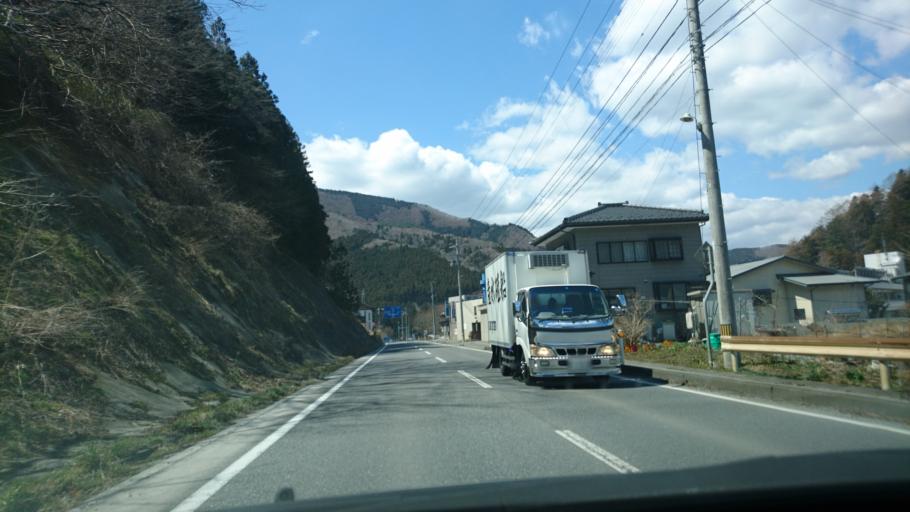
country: JP
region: Iwate
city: Ofunato
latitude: 39.1364
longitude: 141.5820
